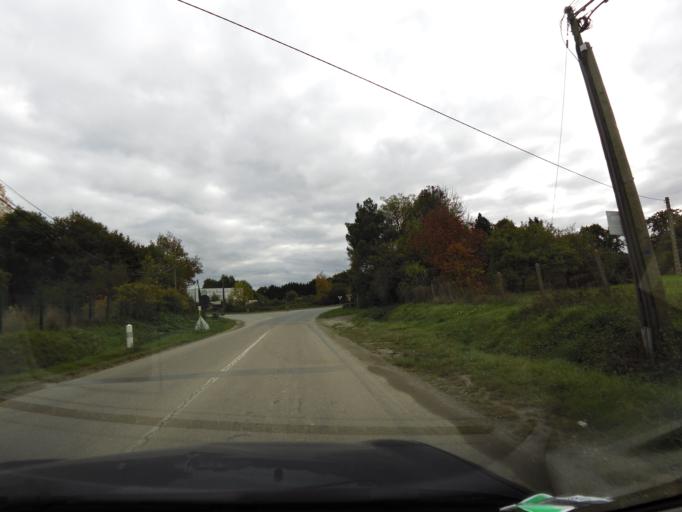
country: FR
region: Brittany
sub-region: Departement d'Ille-et-Vilaine
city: Chantepie
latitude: 48.0820
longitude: -1.6048
